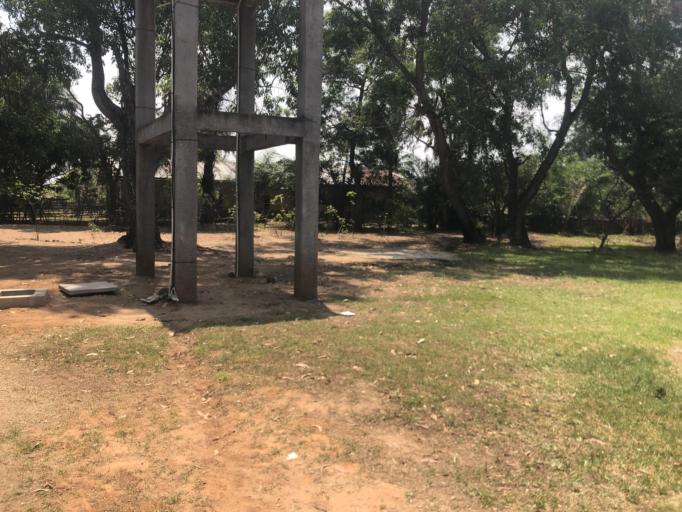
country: CD
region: Bandundu
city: Kikwit
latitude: -5.0708
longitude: 18.8474
